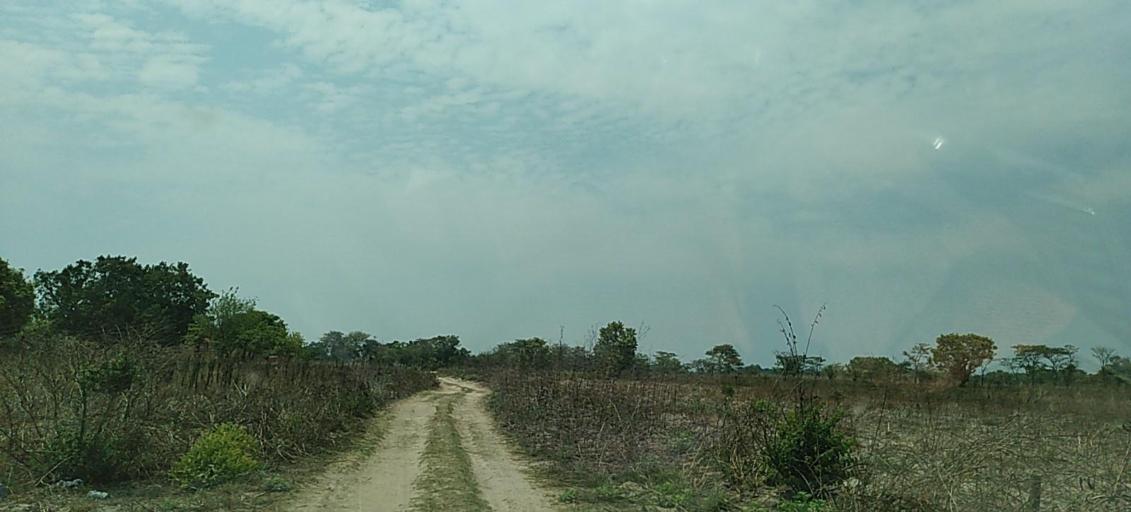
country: ZM
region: Copperbelt
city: Kalulushi
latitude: -12.9352
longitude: 28.1133
